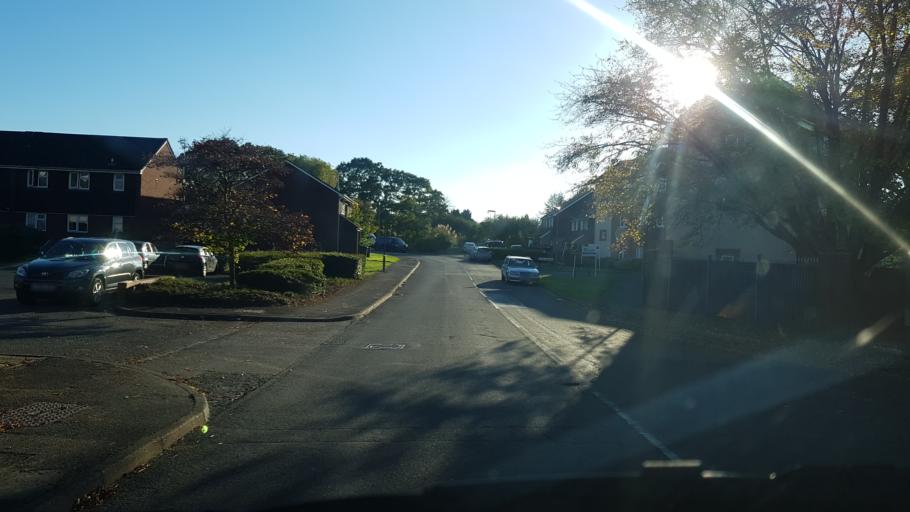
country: GB
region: England
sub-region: Surrey
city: Guildford
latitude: 51.2500
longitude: -0.6099
